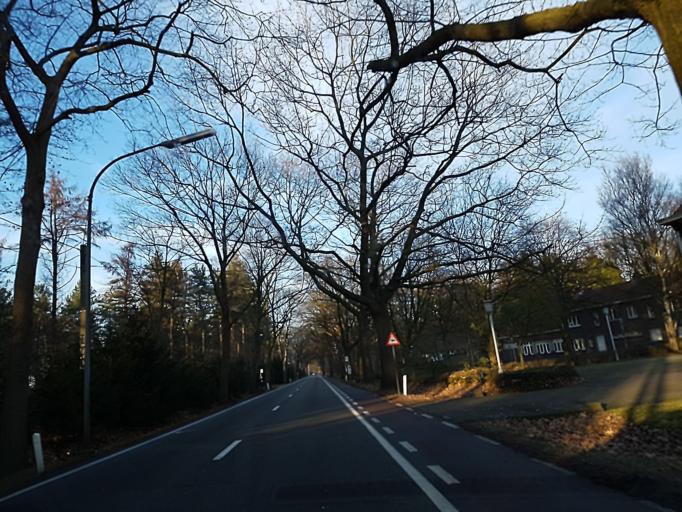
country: NL
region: North Brabant
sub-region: Gemeente Goirle
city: Goirle
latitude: 51.4619
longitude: 5.0444
